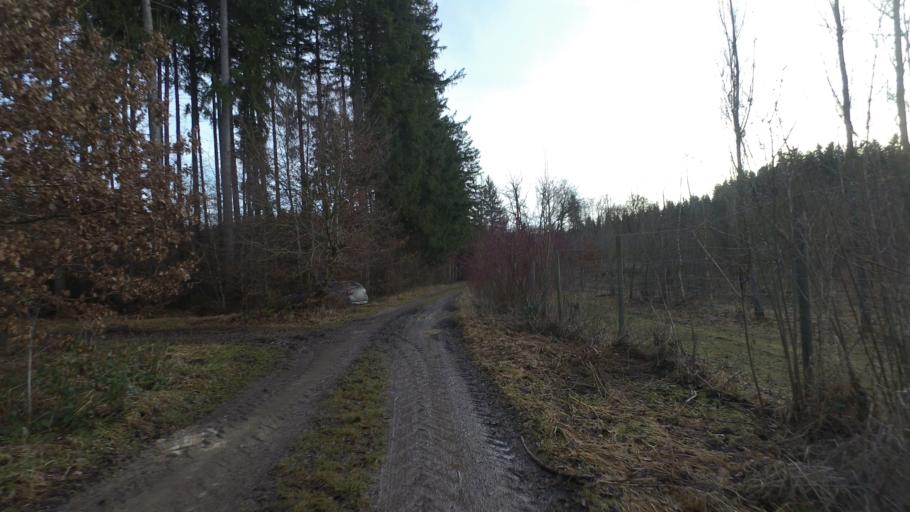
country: DE
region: Bavaria
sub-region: Upper Bavaria
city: Chieming
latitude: 47.8799
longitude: 12.5441
